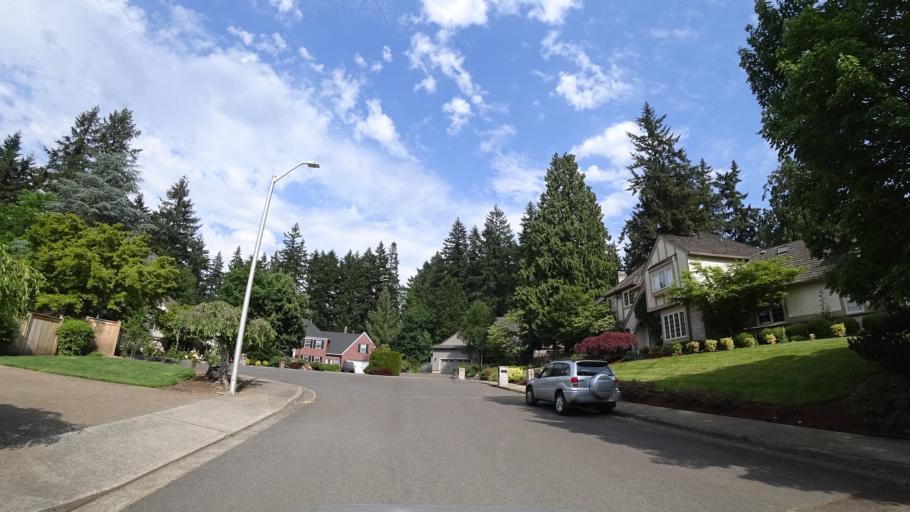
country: US
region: Oregon
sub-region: Washington County
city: Garden Home-Whitford
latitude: 45.4597
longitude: -122.7429
